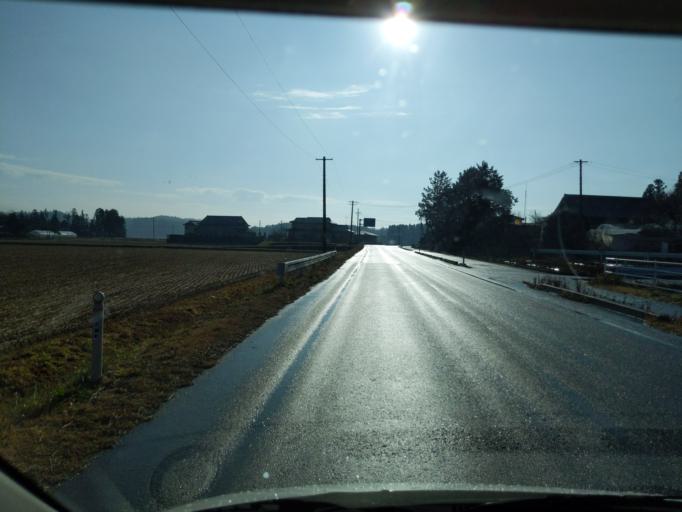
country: JP
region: Iwate
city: Ichinoseki
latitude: 38.7699
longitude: 141.1803
